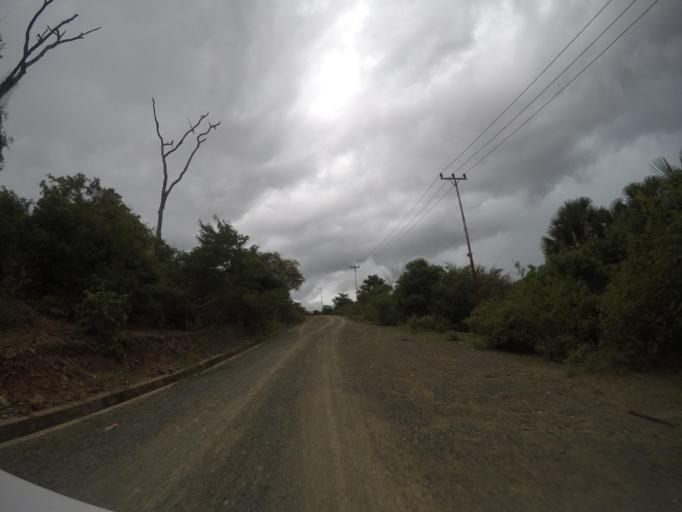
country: TL
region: Bobonaro
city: Maliana
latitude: -8.8520
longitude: 125.0676
